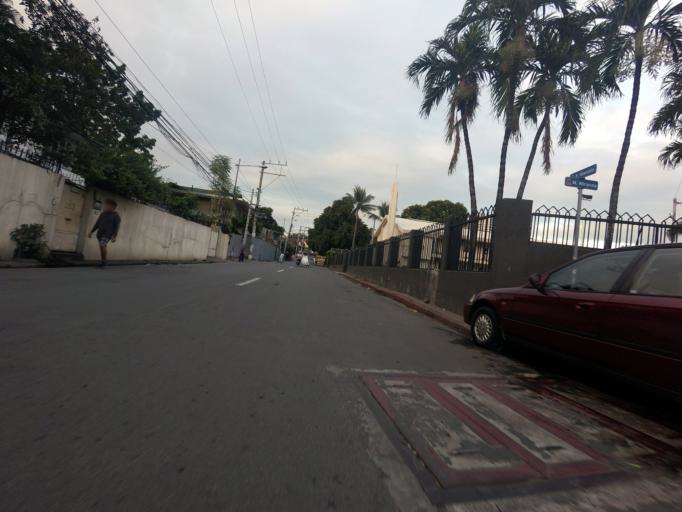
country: PH
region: Metro Manila
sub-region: San Juan
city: San Juan
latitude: 14.5986
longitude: 121.0328
